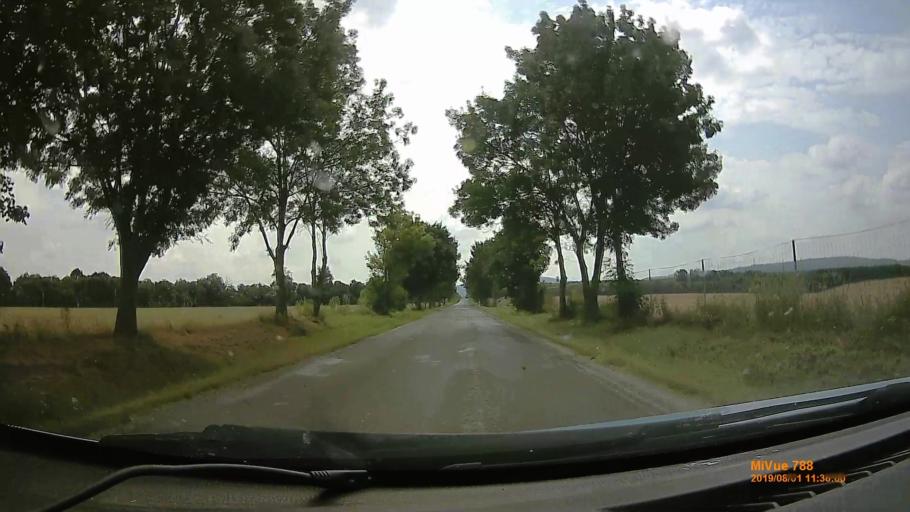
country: HU
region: Baranya
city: Villany
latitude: 45.9217
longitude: 18.3721
